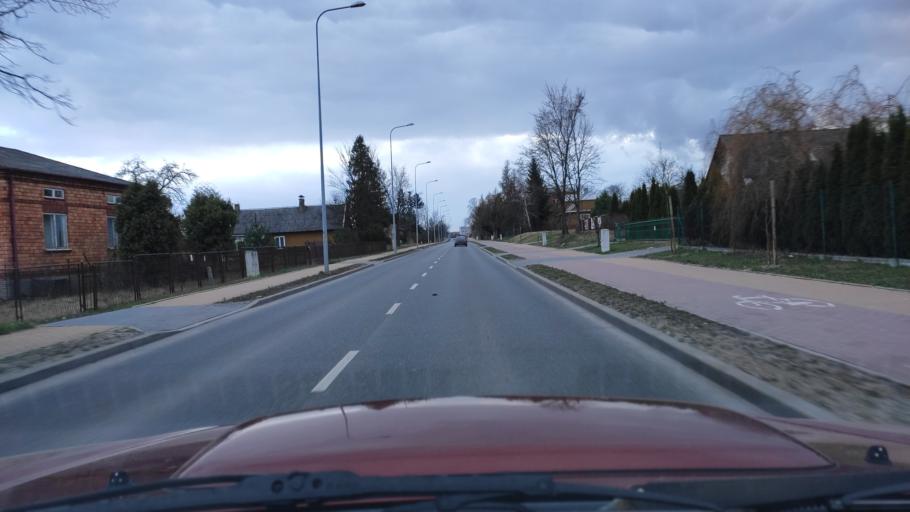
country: PL
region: Masovian Voivodeship
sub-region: Powiat zwolenski
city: Zwolen
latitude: 51.3651
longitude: 21.5843
